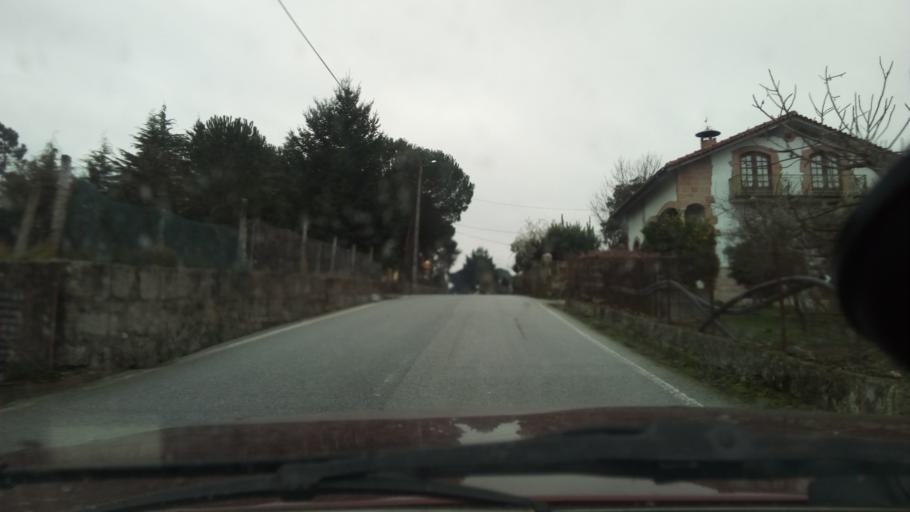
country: PT
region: Viseu
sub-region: Mangualde
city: Mangualde
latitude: 40.6034
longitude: -7.8199
